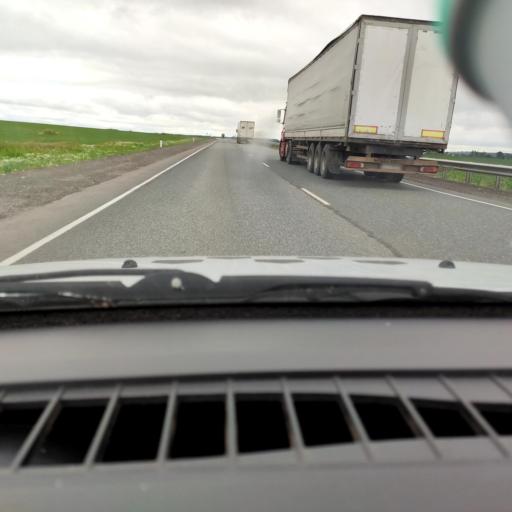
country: RU
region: Udmurtiya
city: Alnashi
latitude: 56.1111
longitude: 52.4607
